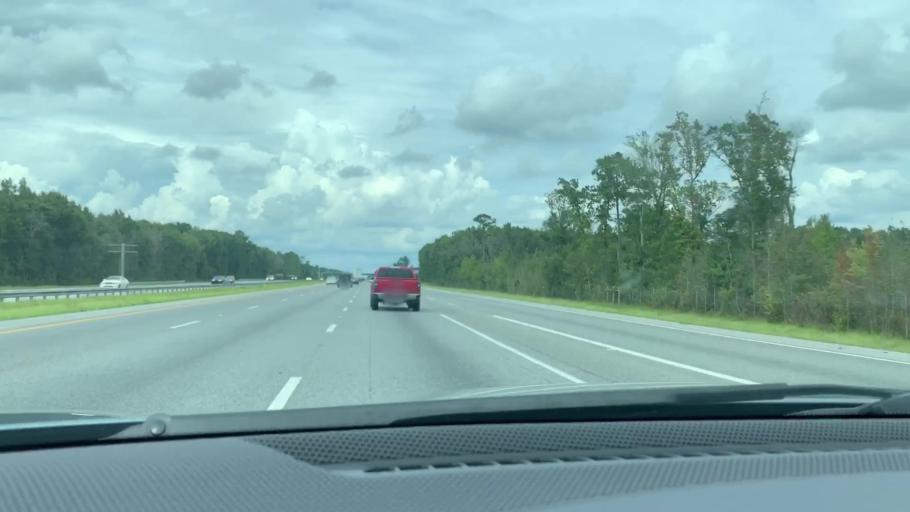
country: US
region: Georgia
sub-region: McIntosh County
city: Darien
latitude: 31.4853
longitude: -81.4470
